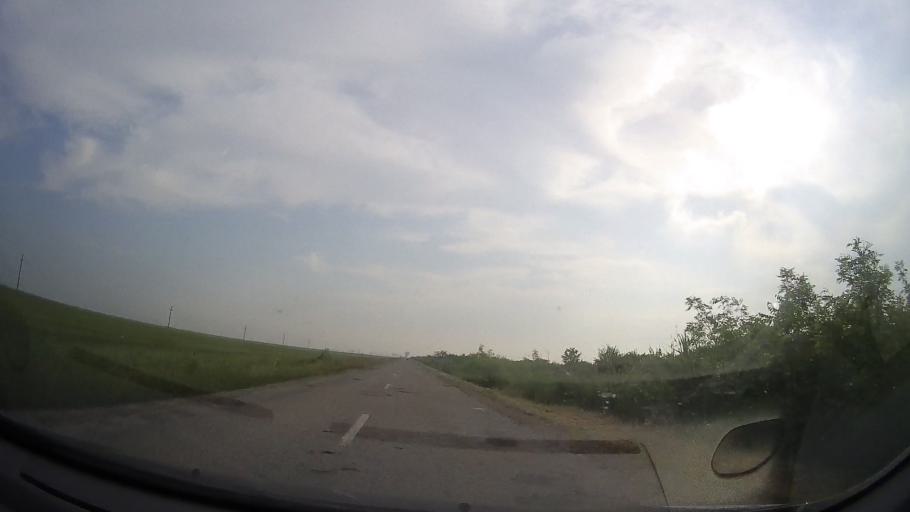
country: RO
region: Timis
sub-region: Comuna Giulvaz
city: Giulvaz
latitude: 45.5738
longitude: 21.0134
